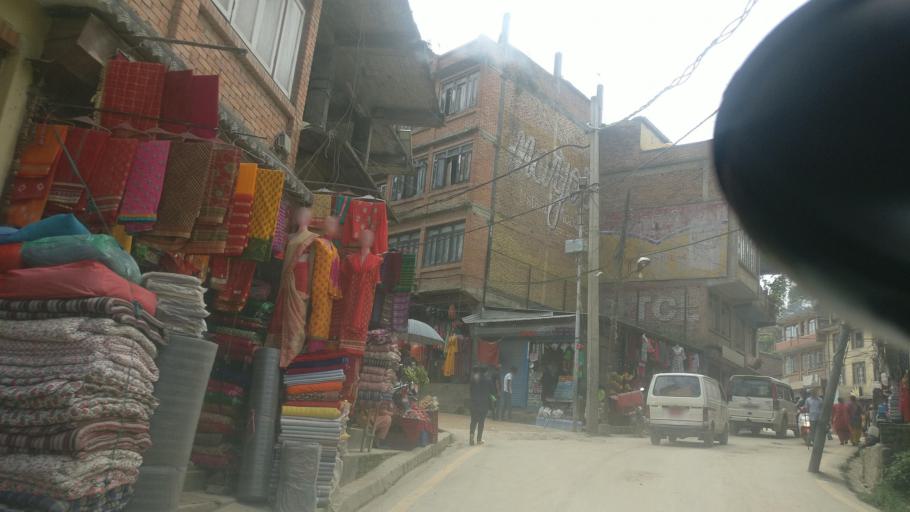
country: NP
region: Central Region
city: Panaoti
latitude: 27.5860
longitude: 85.5134
